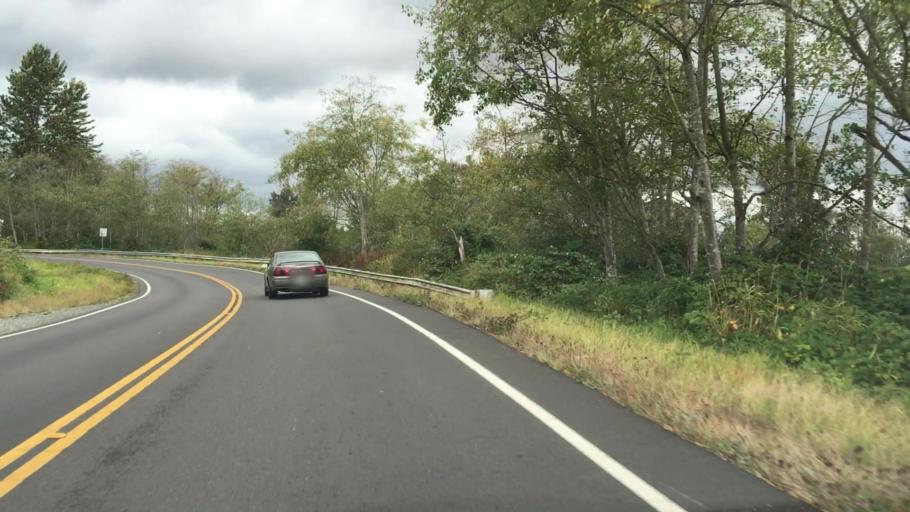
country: US
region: Washington
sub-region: Snohomish County
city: Everett
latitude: 47.9458
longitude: -122.1773
